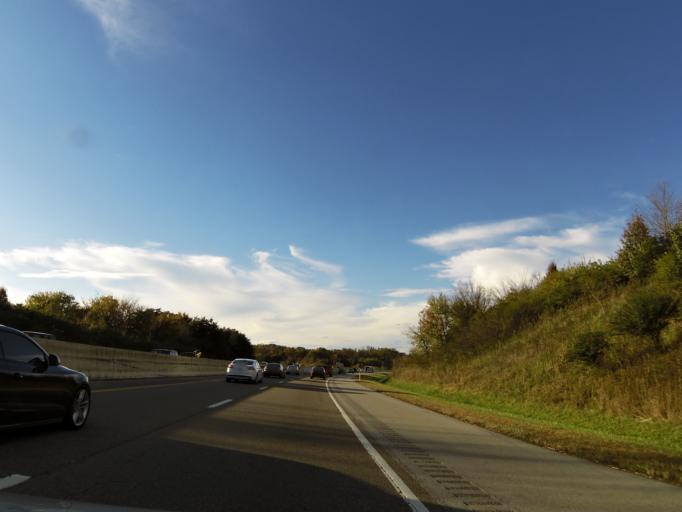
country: US
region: Tennessee
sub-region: Blount County
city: Louisville
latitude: 35.8517
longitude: -84.0199
